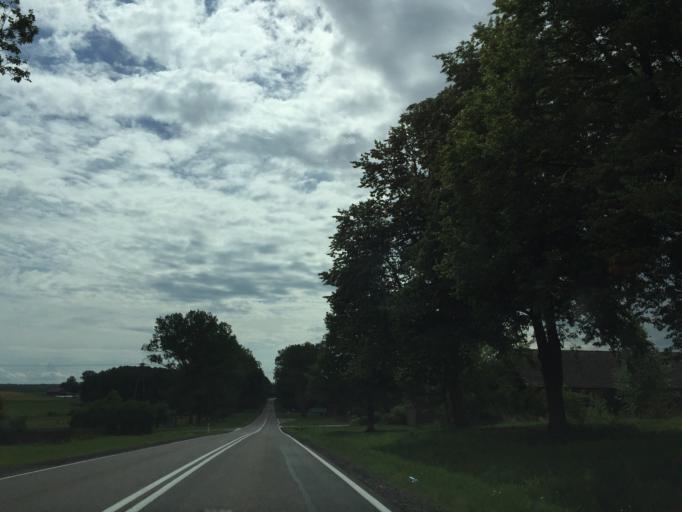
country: PL
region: Podlasie
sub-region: Powiat bielski
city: Bocki
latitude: 52.6106
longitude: 22.9874
